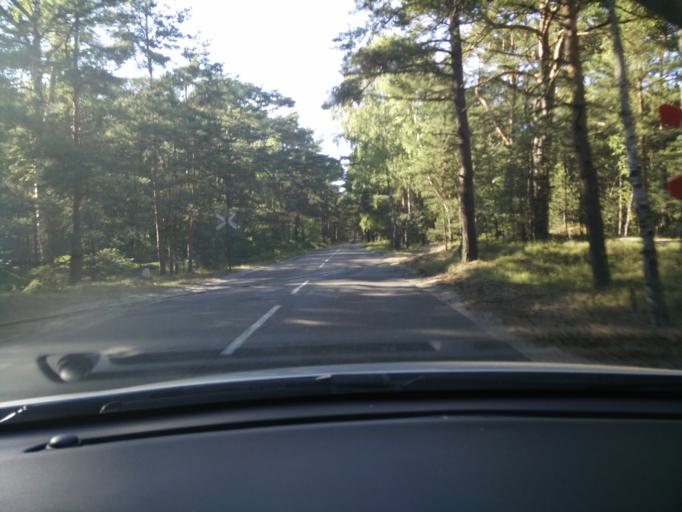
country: PL
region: Pomeranian Voivodeship
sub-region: Powiat pucki
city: Hel
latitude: 54.6381
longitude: 18.7763
